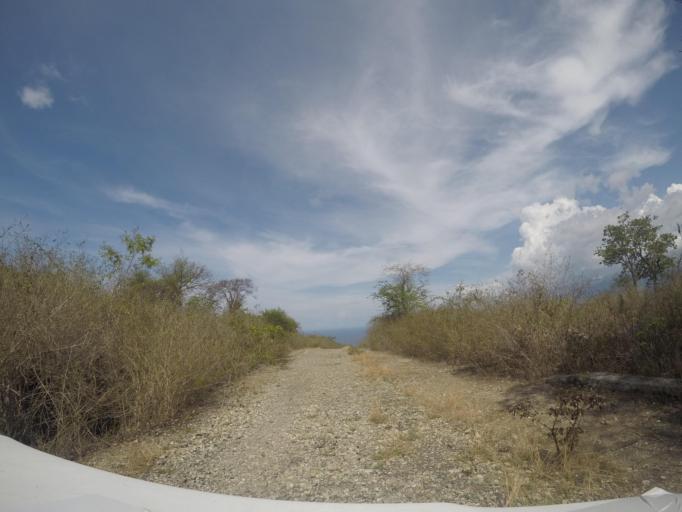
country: TL
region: Baucau
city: Baucau
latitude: -8.4666
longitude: 126.4686
